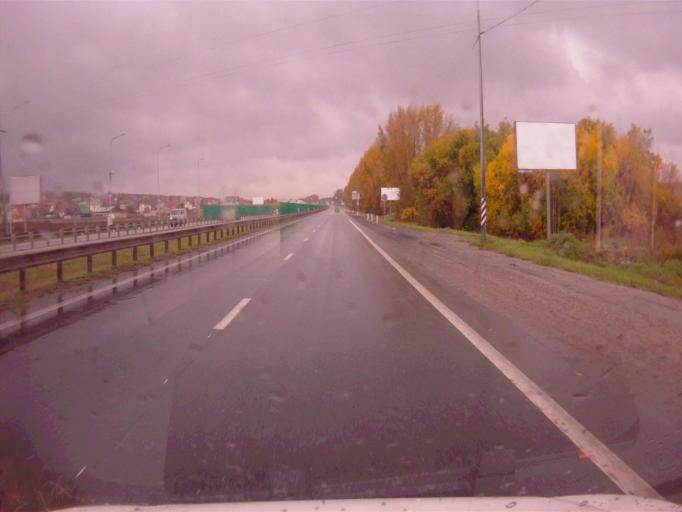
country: RU
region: Chelyabinsk
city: Dolgoderevenskoye
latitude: 55.2777
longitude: 61.3436
